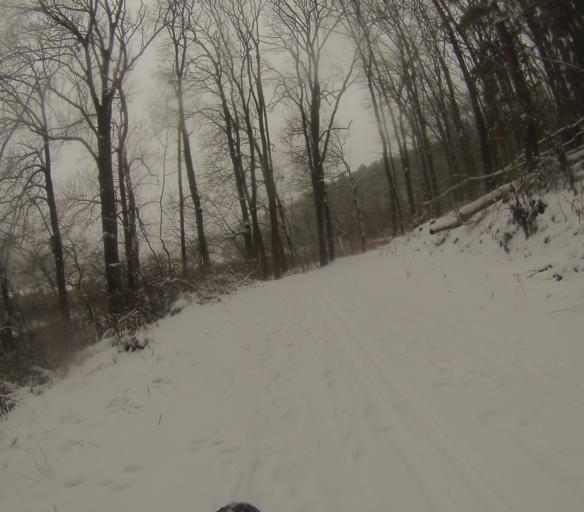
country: CZ
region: South Moravian
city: Strelice
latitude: 49.1397
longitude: 16.4887
